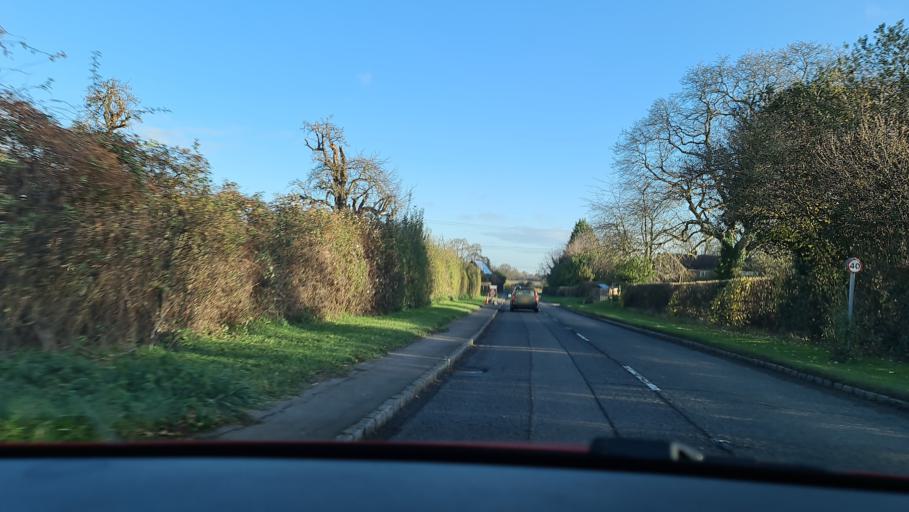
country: GB
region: England
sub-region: Buckinghamshire
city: Weston Turville
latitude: 51.7674
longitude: -0.7816
